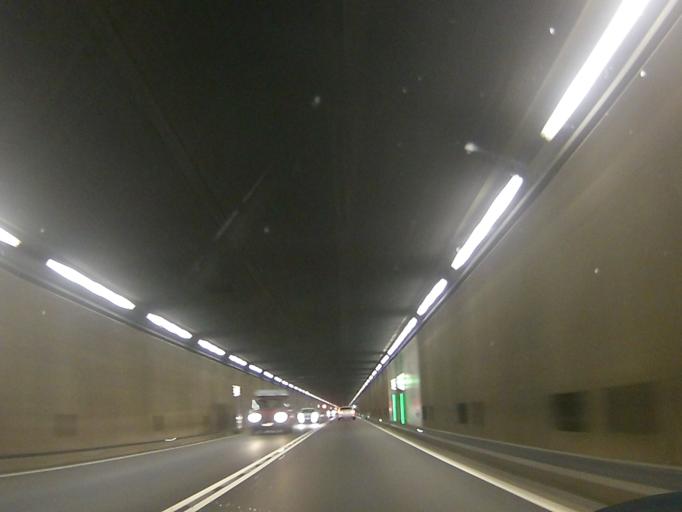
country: CH
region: Ticino
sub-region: Leventina District
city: Airolo
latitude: 46.5471
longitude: 8.5847
